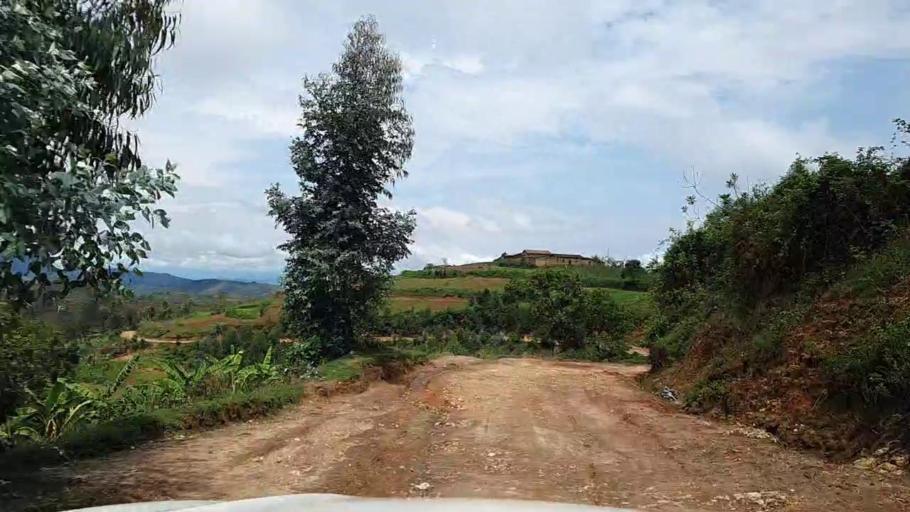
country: RW
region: Southern Province
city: Gikongoro
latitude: -2.3428
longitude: 29.5115
